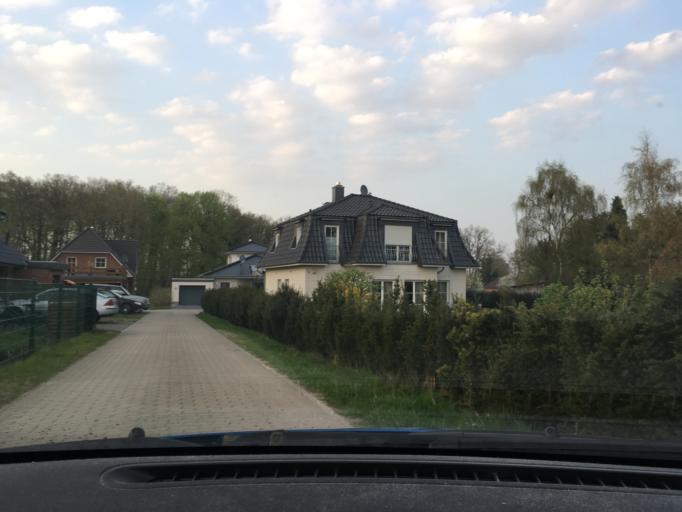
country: DE
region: Lower Saxony
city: Embsen
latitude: 53.1952
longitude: 10.3220
